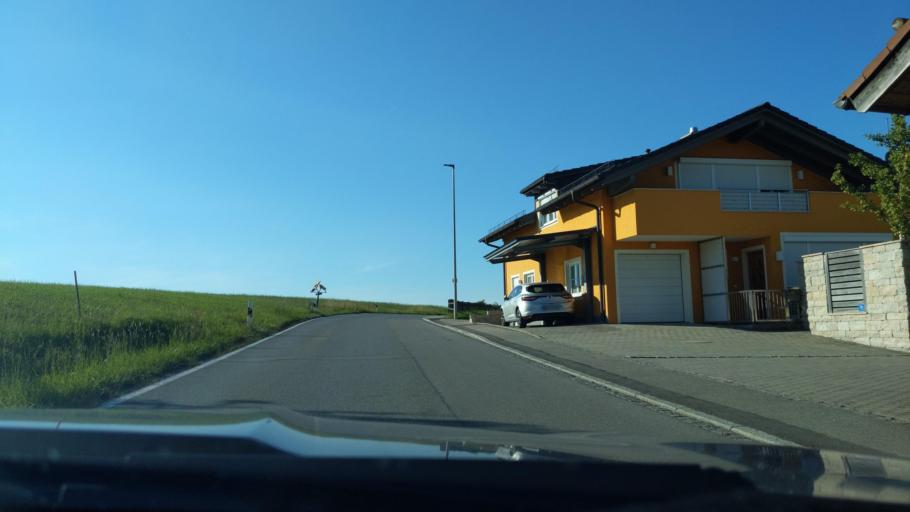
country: DE
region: Bavaria
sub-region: Upper Bavaria
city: Assling
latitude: 48.0004
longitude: 11.9721
